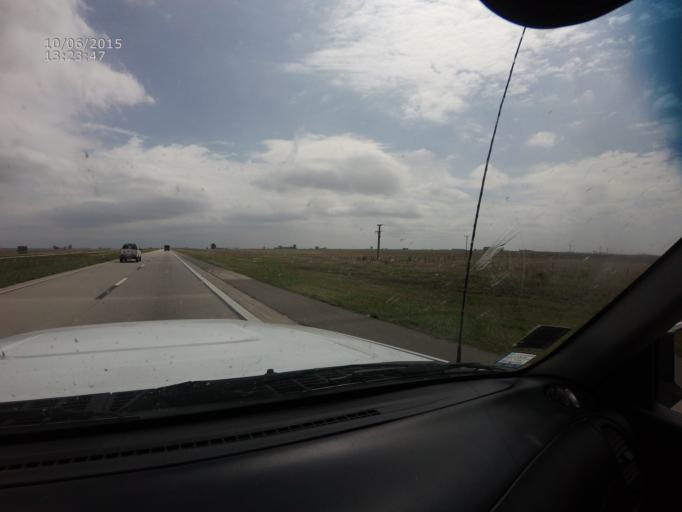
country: AR
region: Cordoba
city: Marcos Juarez
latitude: -32.6595
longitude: -62.1243
